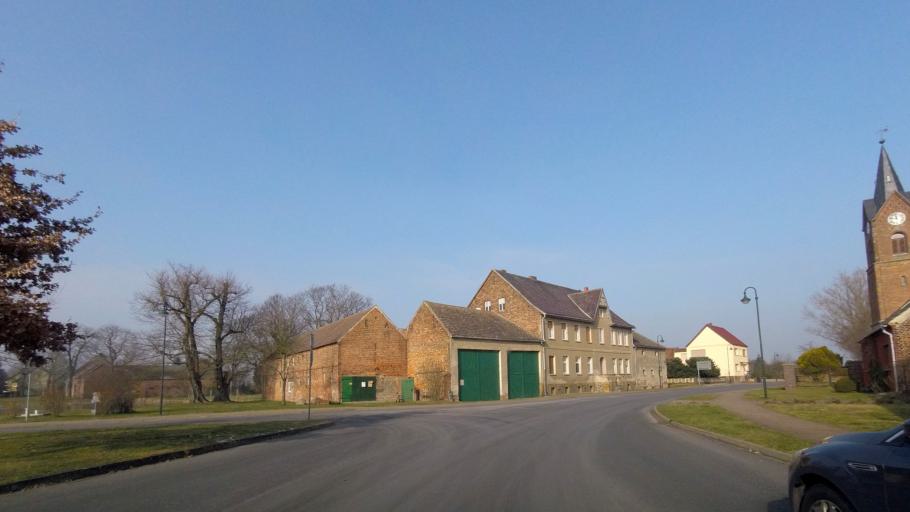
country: DE
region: Brandenburg
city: Niedergorsdorf
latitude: 51.9300
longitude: 13.0343
